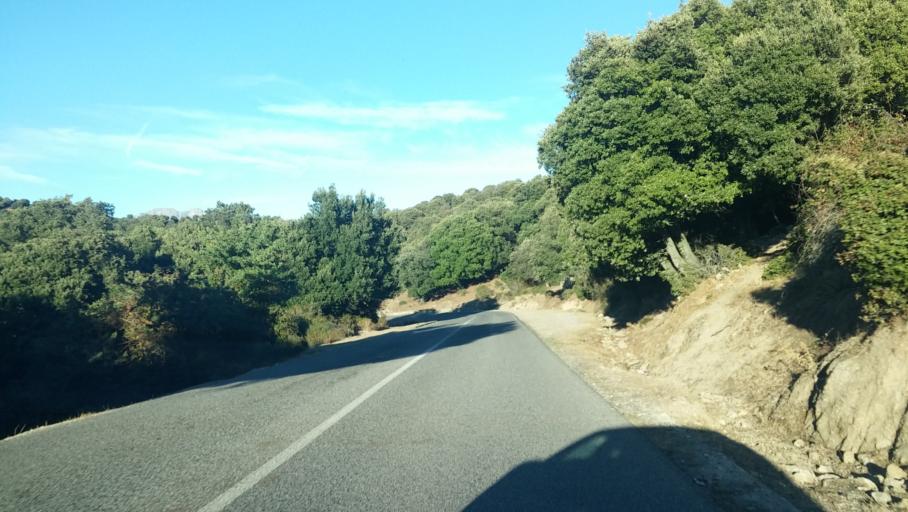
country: IT
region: Sardinia
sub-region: Provincia di Nuoro
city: Orgosolo
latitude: 40.1901
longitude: 9.3520
